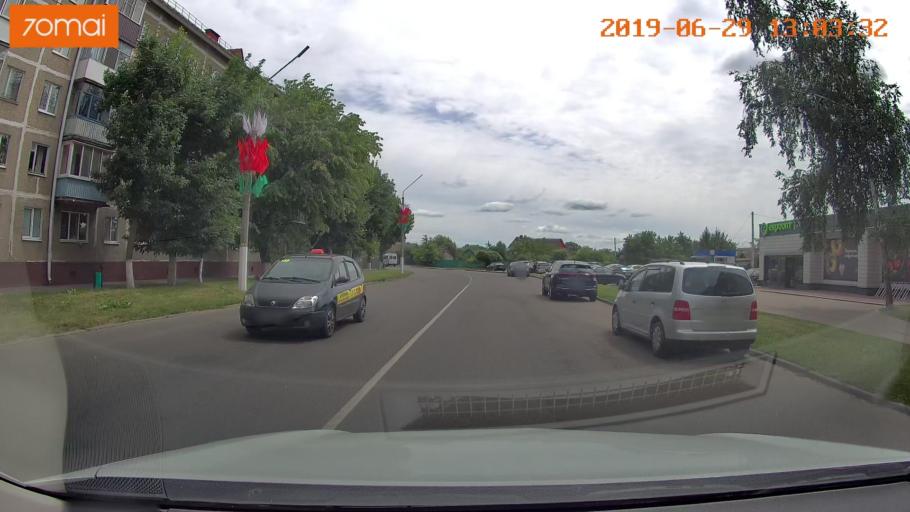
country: BY
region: Minsk
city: Slutsk
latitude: 53.0317
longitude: 27.5621
